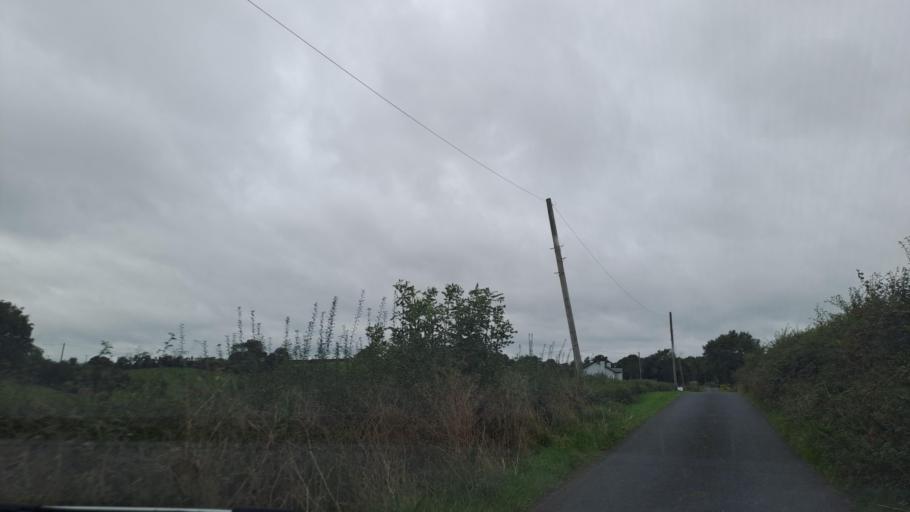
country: IE
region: Ulster
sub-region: An Cabhan
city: Kingscourt
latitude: 54.0053
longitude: -6.8620
